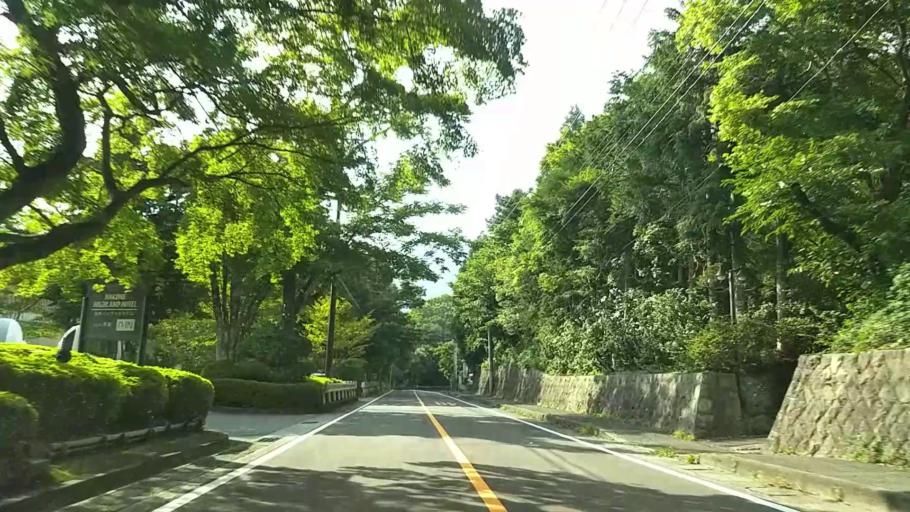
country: JP
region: Kanagawa
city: Hakone
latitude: 35.2679
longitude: 139.0157
